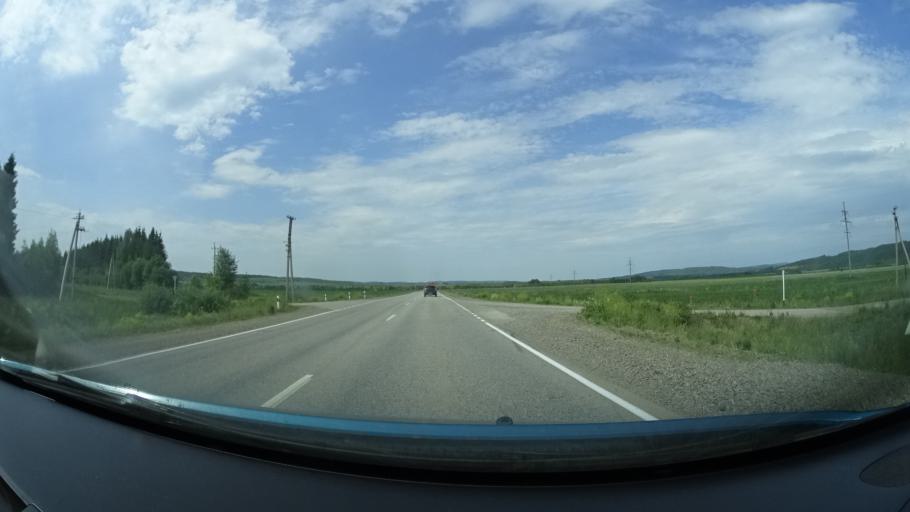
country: RU
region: Perm
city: Barda
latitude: 57.0159
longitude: 55.5589
